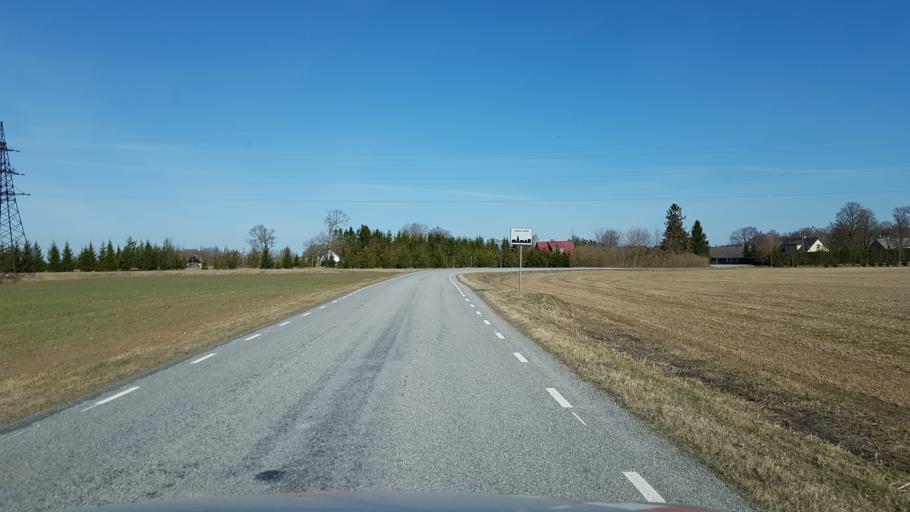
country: EE
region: Laeaene-Virumaa
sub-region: Vinni vald
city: Vinni
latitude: 59.2874
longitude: 26.3851
